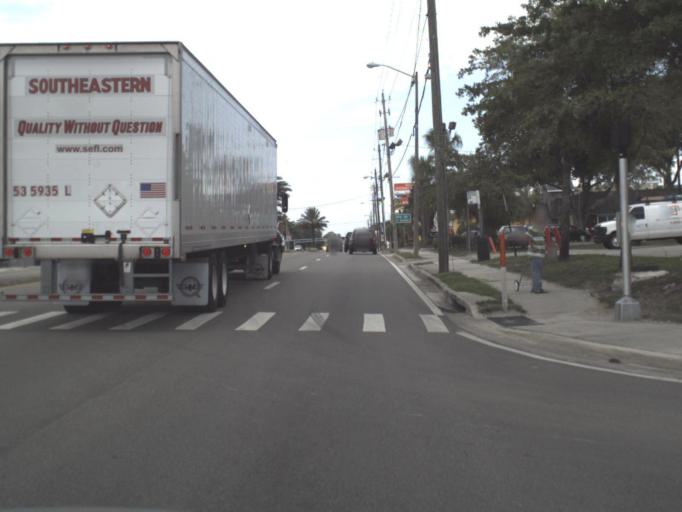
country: US
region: Florida
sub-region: Hillsborough County
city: University
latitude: 28.0325
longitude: -82.4305
